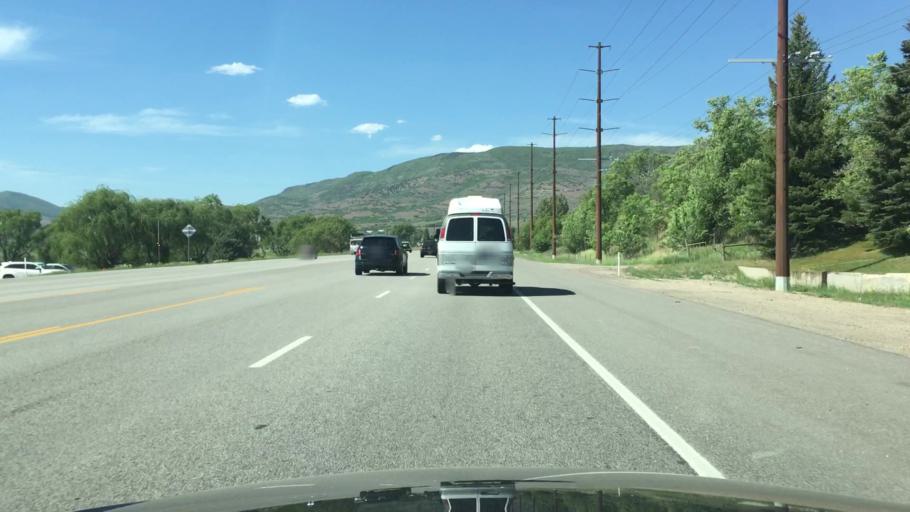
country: US
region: Utah
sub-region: Wasatch County
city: Heber
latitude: 40.5216
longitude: -111.4108
